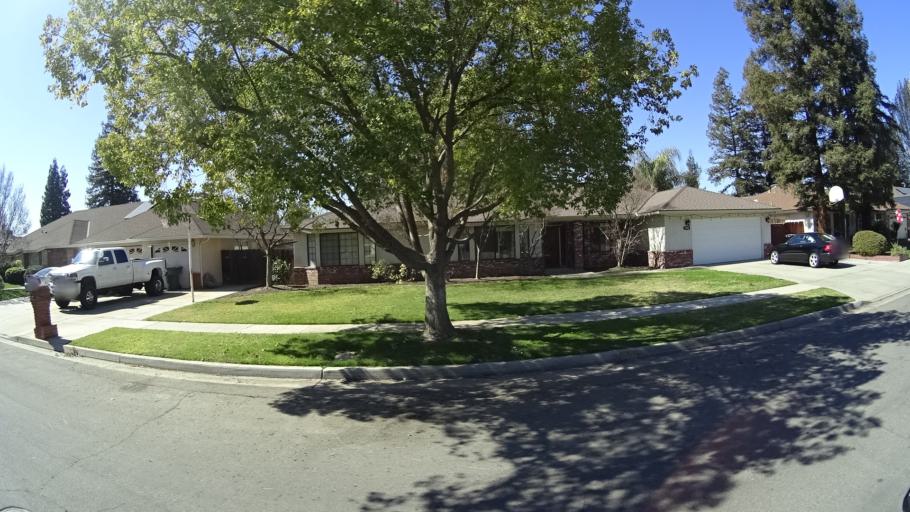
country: US
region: California
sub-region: Fresno County
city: Clovis
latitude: 36.8460
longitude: -119.7499
